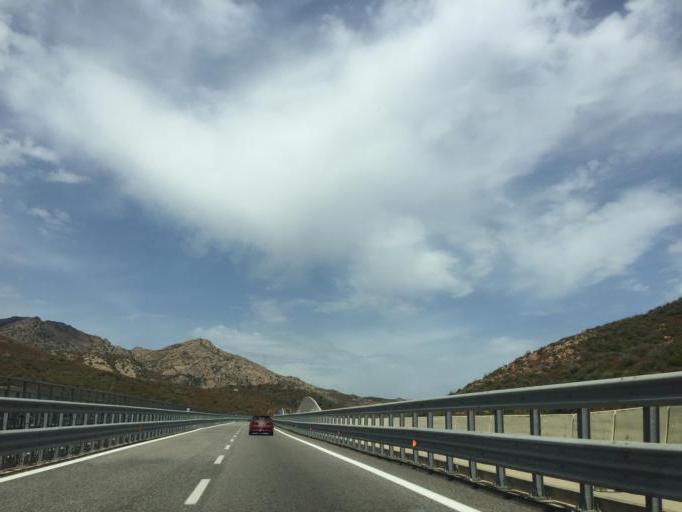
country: IT
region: Sardinia
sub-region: Provincia di Olbia-Tempio
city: San Teodoro
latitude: 40.7722
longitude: 9.6320
